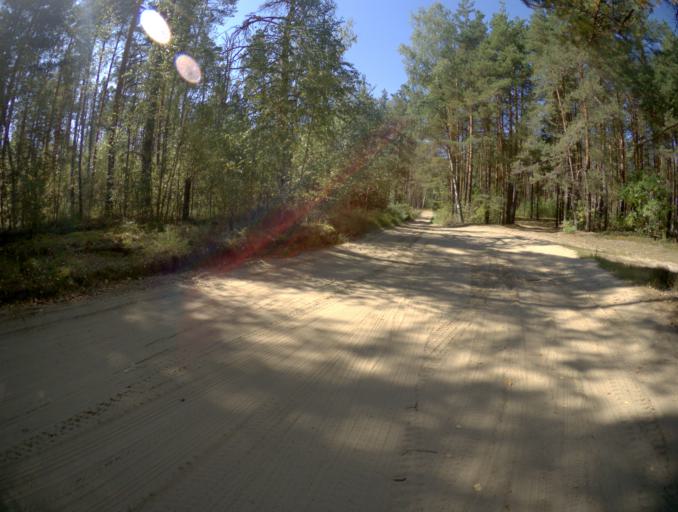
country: RU
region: Vladimir
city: Petushki
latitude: 55.8667
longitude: 39.3208
